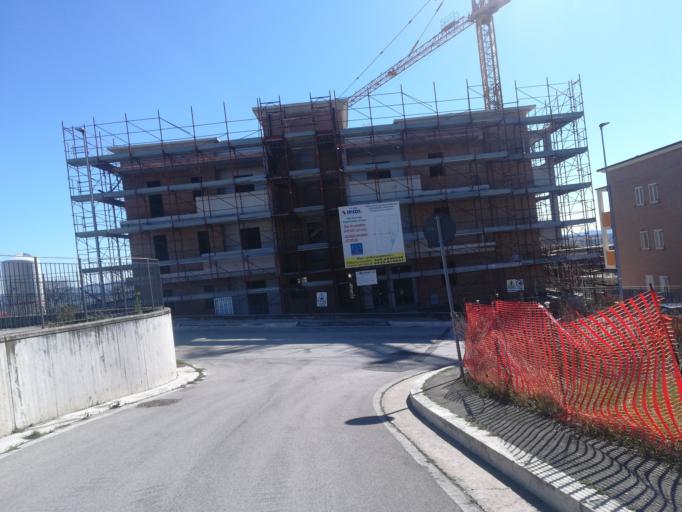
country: IT
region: The Marches
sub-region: Provincia di Macerata
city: Piediripa
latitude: 43.2897
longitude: 13.4756
